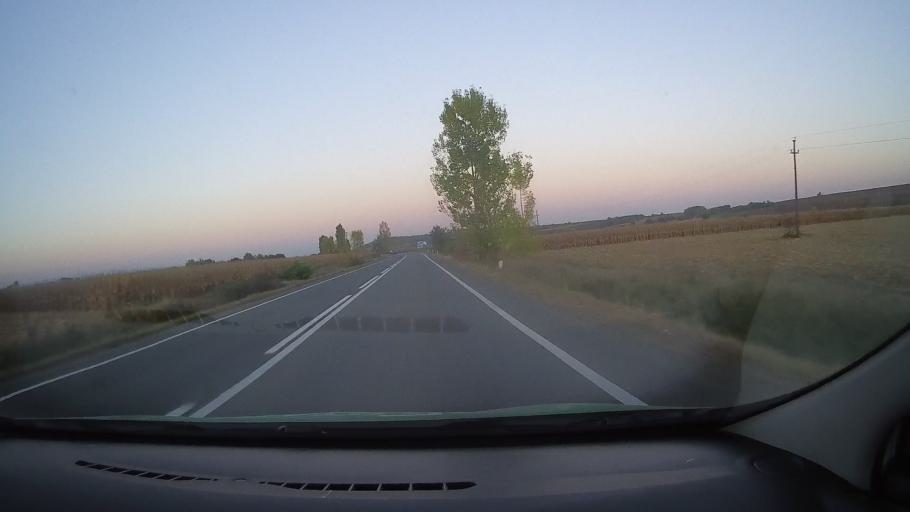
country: RO
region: Bihor
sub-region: Comuna Tarcea
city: Tarcea
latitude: 47.4266
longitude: 22.2005
